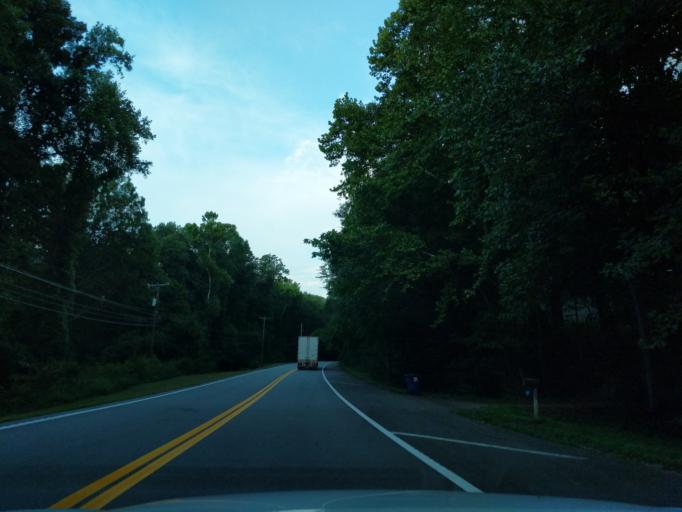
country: US
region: Tennessee
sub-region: Hamilton County
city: Lookout Mountain
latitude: 35.0357
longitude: -85.4237
